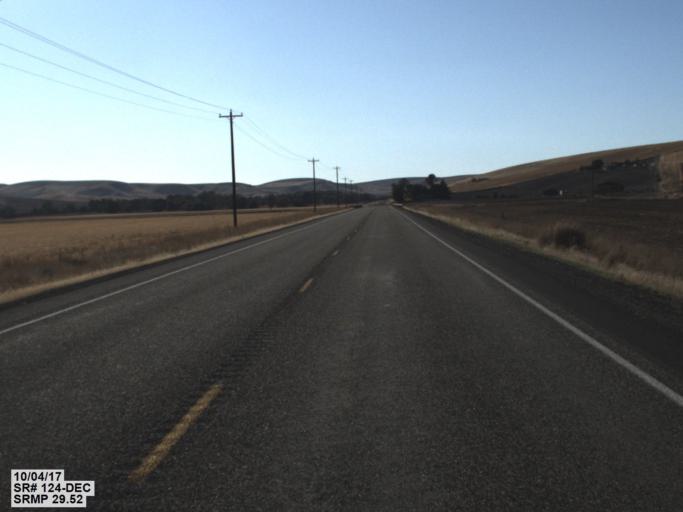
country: US
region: Washington
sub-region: Walla Walla County
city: Garrett
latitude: 46.2959
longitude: -118.4464
